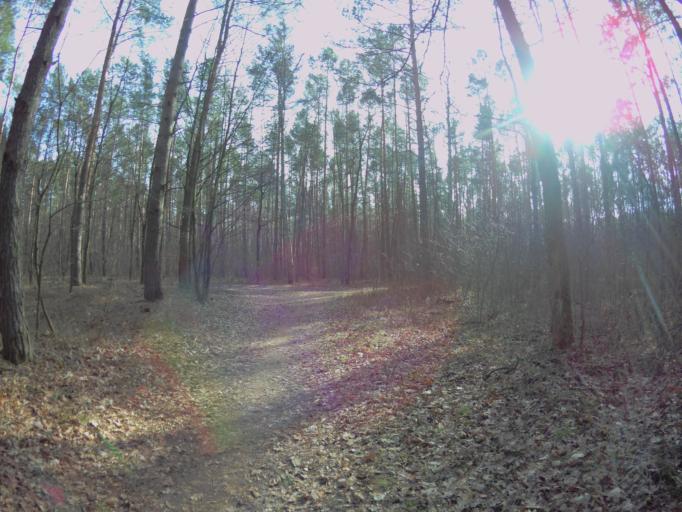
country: PL
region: Subcarpathian Voivodeship
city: Nowa Sarzyna
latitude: 50.3145
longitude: 22.3474
